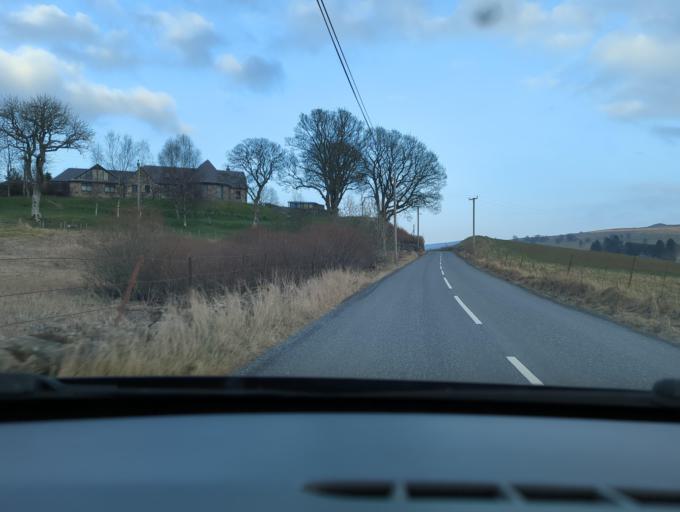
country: GB
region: Scotland
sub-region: Perth and Kinross
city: Aberfeldy
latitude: 56.5277
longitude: -3.7333
